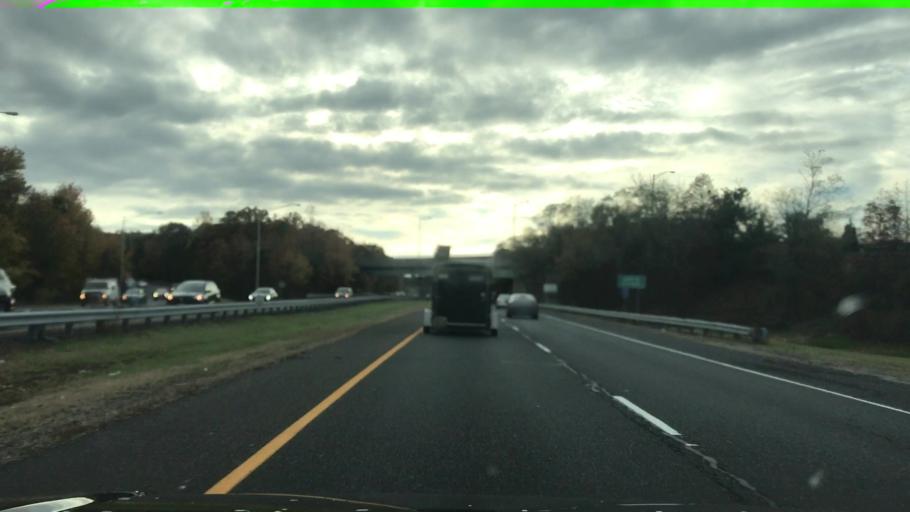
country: US
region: New Jersey
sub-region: Monmouth County
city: Eatontown
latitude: 40.2901
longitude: -74.0720
